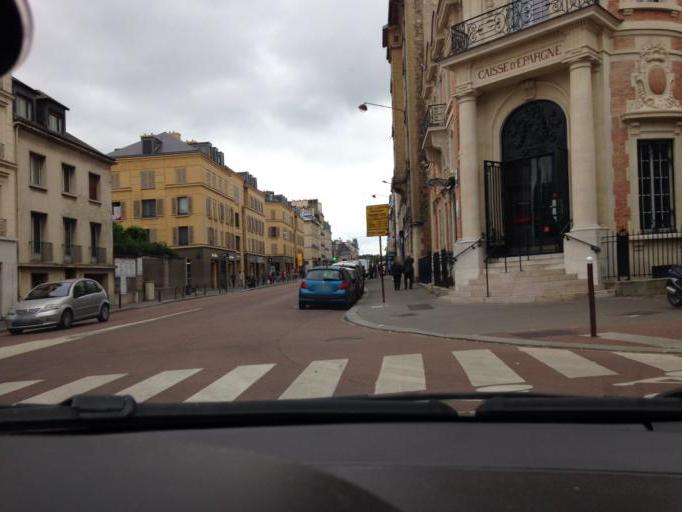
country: FR
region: Ile-de-France
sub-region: Departement des Yvelines
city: Versailles
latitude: 48.8089
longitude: 2.1334
